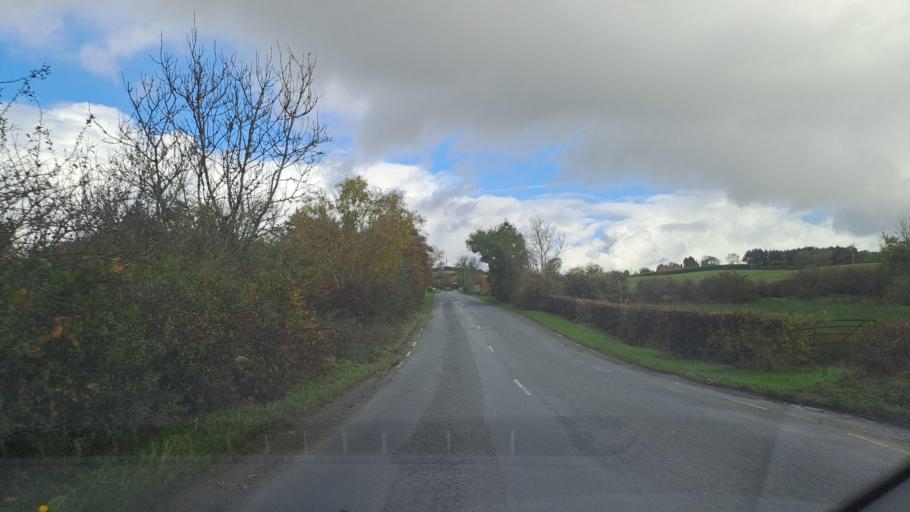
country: IE
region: Ulster
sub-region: An Cabhan
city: Bailieborough
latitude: 53.9036
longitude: -6.9673
